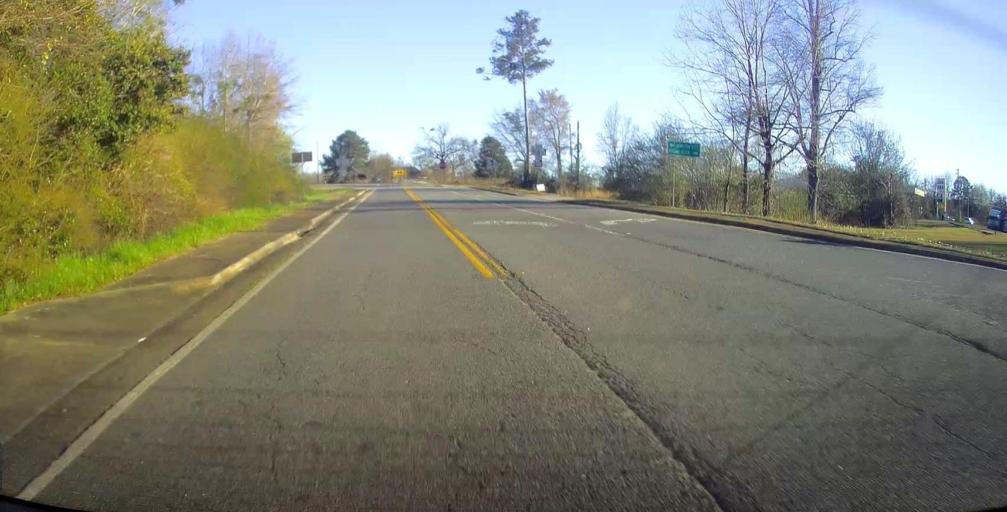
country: US
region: Georgia
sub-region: Talbot County
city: Talbotton
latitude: 32.5792
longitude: -84.5532
